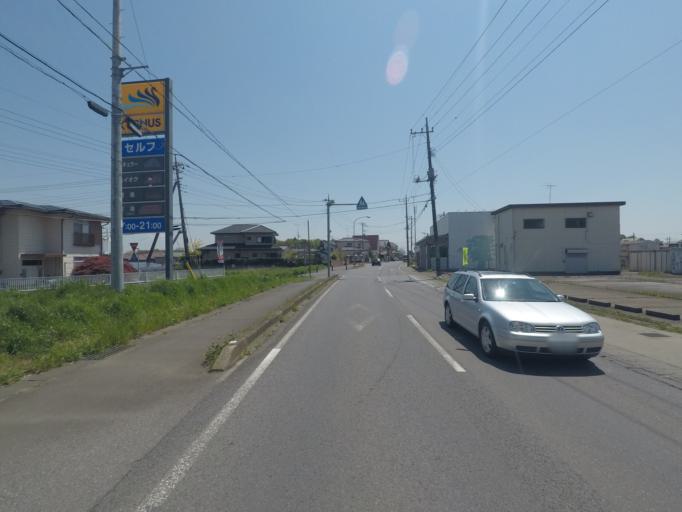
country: JP
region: Ibaraki
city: Ushiku
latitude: 35.9614
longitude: 140.1028
